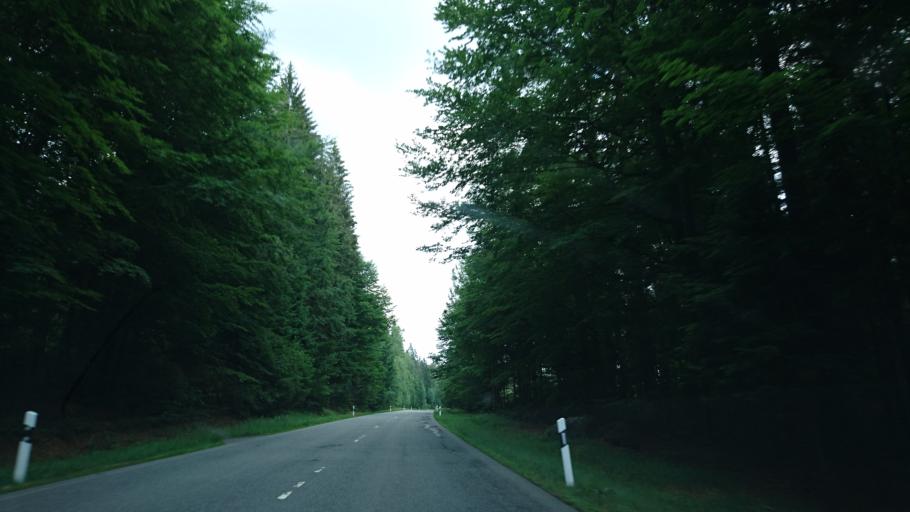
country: DE
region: Bavaria
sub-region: Lower Bavaria
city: Neuschonau
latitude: 48.9211
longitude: 13.4504
